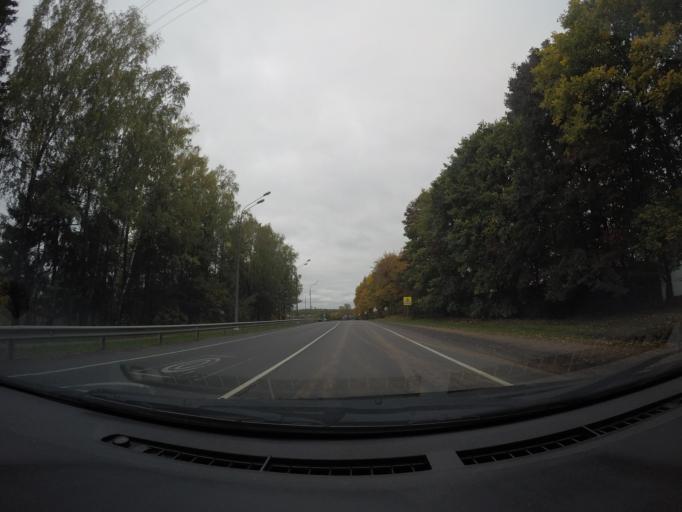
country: RU
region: Moskovskaya
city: Ruza
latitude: 55.7377
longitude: 36.2224
